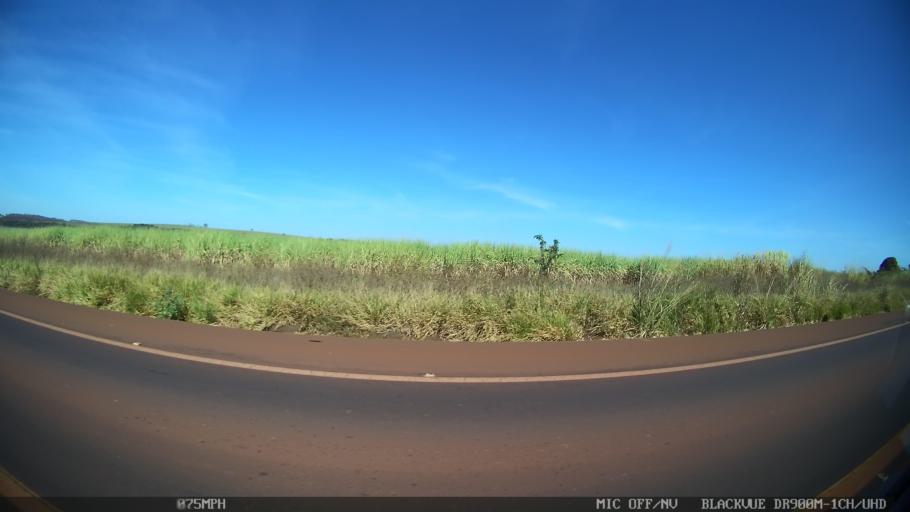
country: BR
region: Sao Paulo
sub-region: Sao Joaquim Da Barra
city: Sao Joaquim da Barra
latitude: -20.5398
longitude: -47.8148
